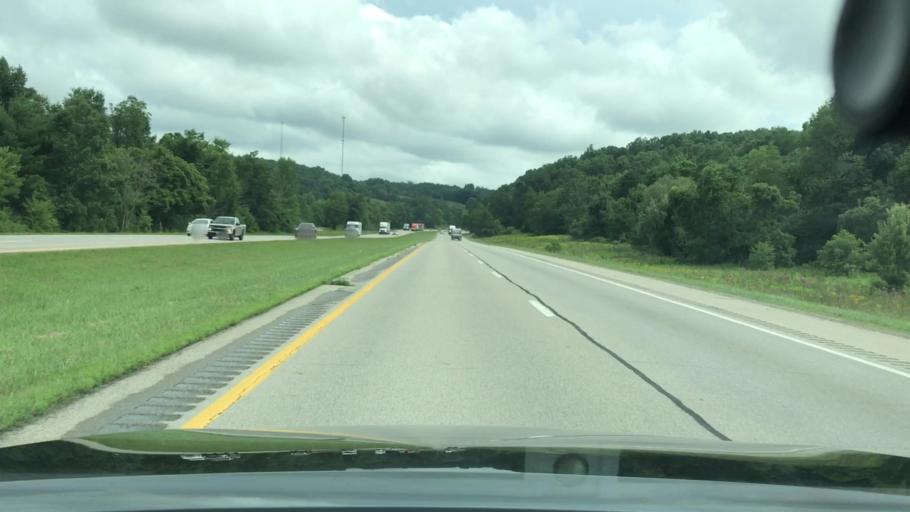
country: US
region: Ohio
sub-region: Jackson County
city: Oak Hill
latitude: 38.9394
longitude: -82.4717
